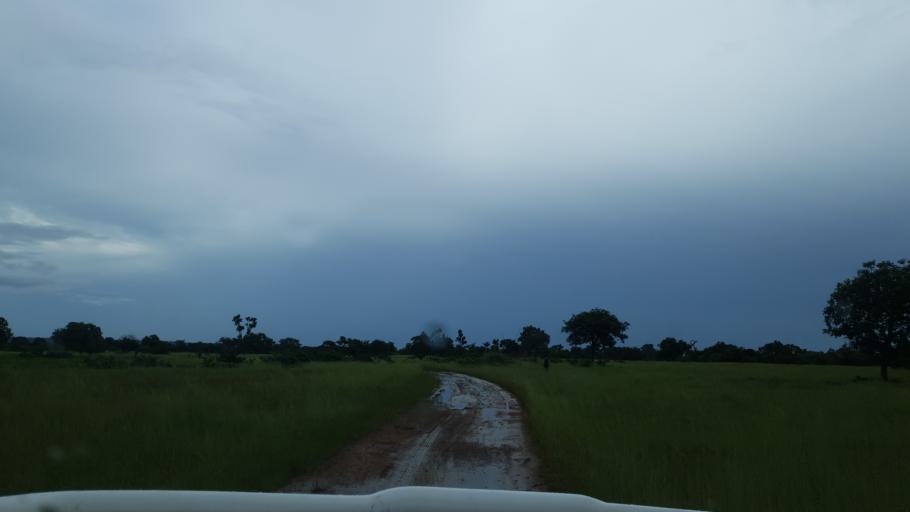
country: ML
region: Sikasso
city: Sikasso
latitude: 11.6298
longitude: -6.0275
